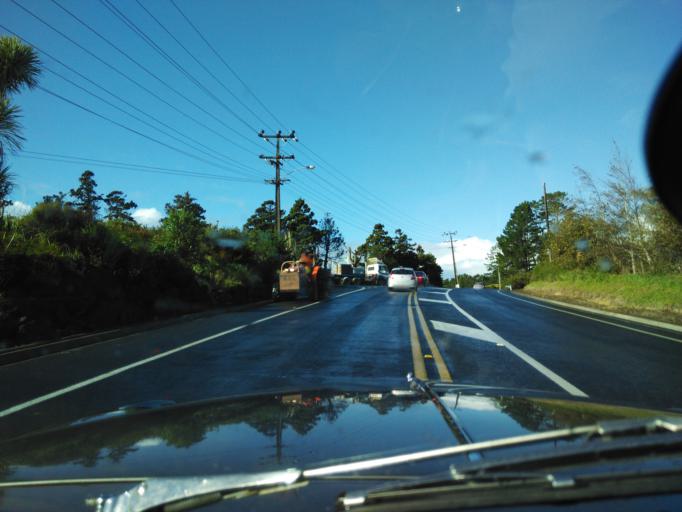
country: NZ
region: Auckland
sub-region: Auckland
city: Rothesay Bay
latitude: -36.6326
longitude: 174.6140
